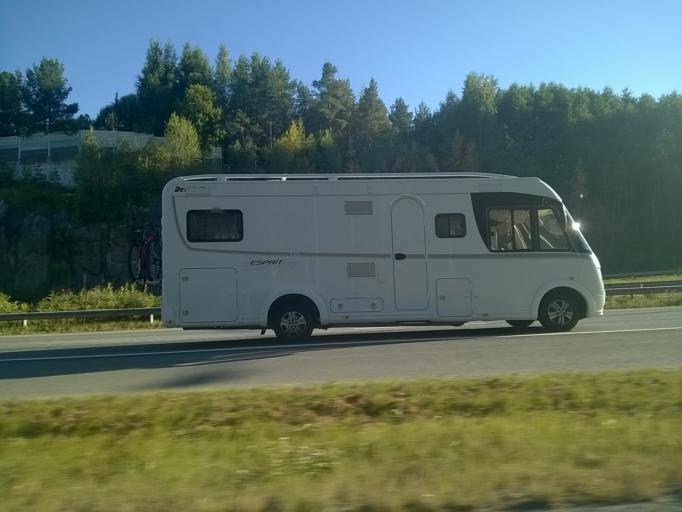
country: FI
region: Pirkanmaa
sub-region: Tampere
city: Tampere
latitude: 61.4704
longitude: 23.8468
